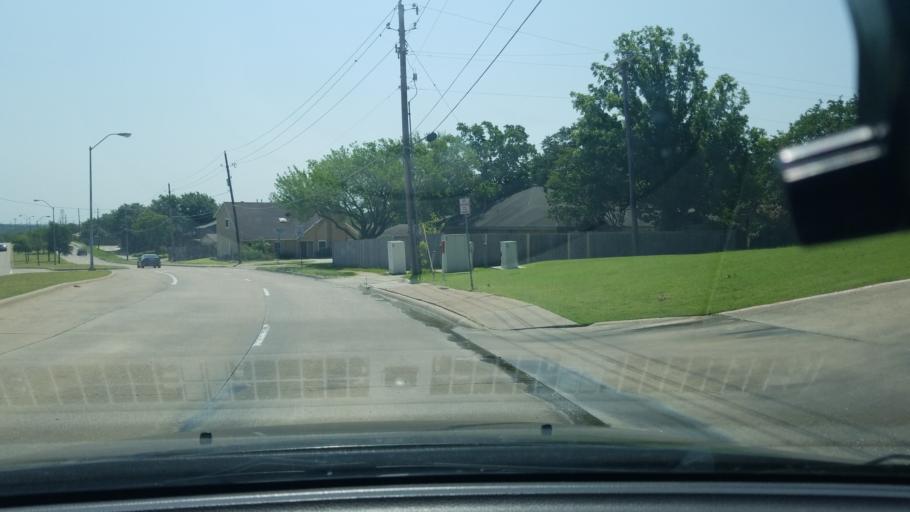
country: US
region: Texas
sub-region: Dallas County
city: Sunnyvale
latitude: 32.8312
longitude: -96.6108
